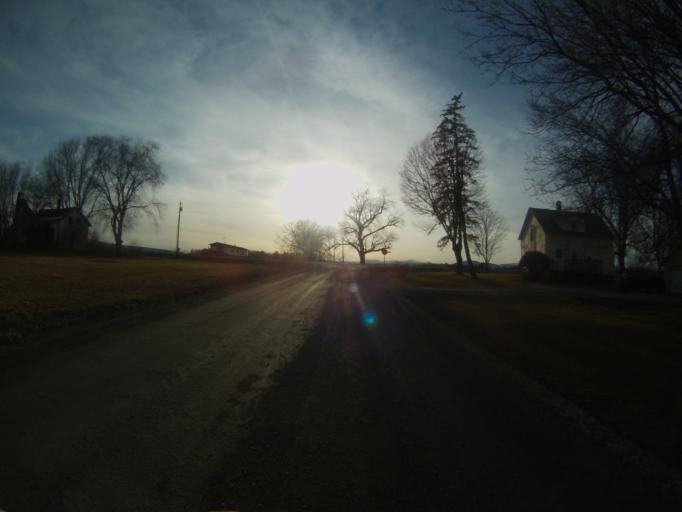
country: US
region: New York
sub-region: Essex County
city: Port Henry
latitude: 44.0532
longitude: -73.3757
